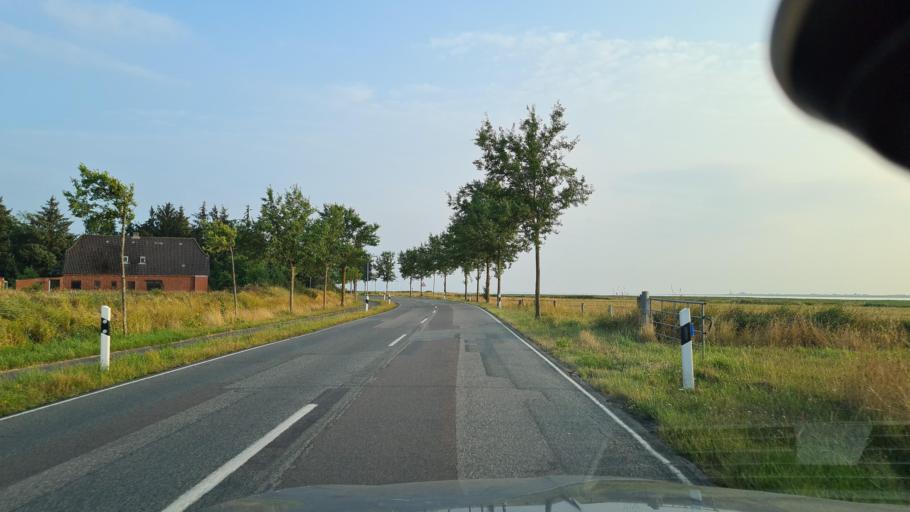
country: DE
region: Schleswig-Holstein
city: Schobull
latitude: 54.5181
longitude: 8.9959
